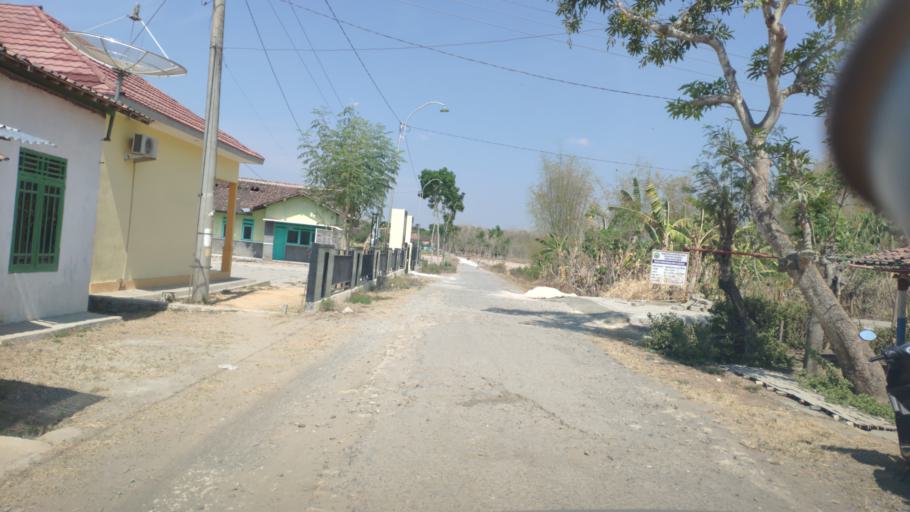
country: ID
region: Central Java
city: Kulonkali
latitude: -6.9942
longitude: 111.3750
